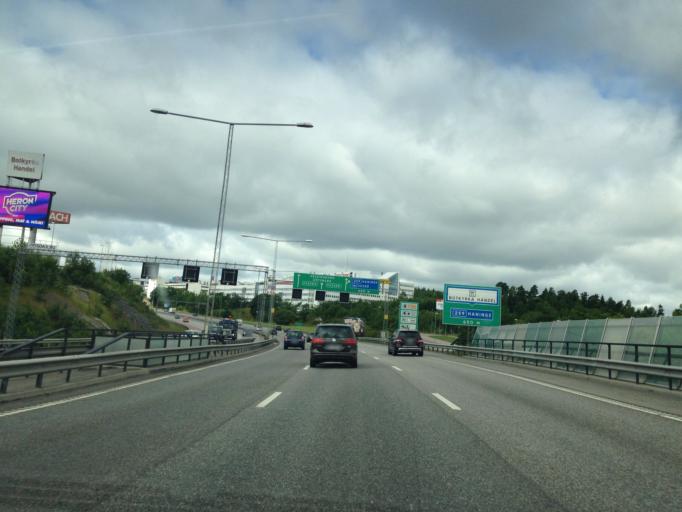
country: SE
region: Stockholm
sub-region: Botkyrka Kommun
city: Fittja
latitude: 59.2548
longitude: 17.8688
